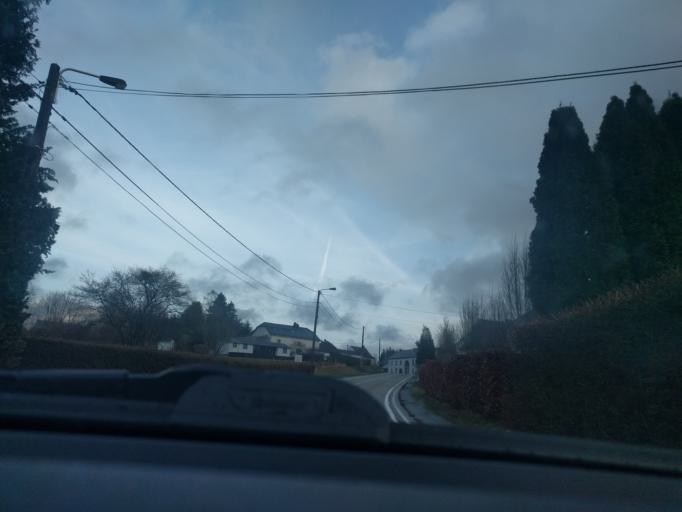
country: BE
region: Wallonia
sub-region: Province du Luxembourg
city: Gouvy
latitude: 50.1872
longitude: 5.9733
